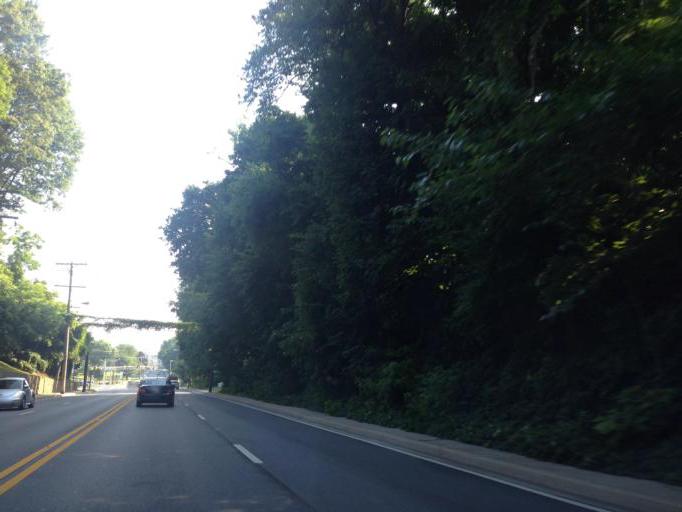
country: US
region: Maryland
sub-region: Baltimore County
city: Towson
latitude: 39.3880
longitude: -76.6059
